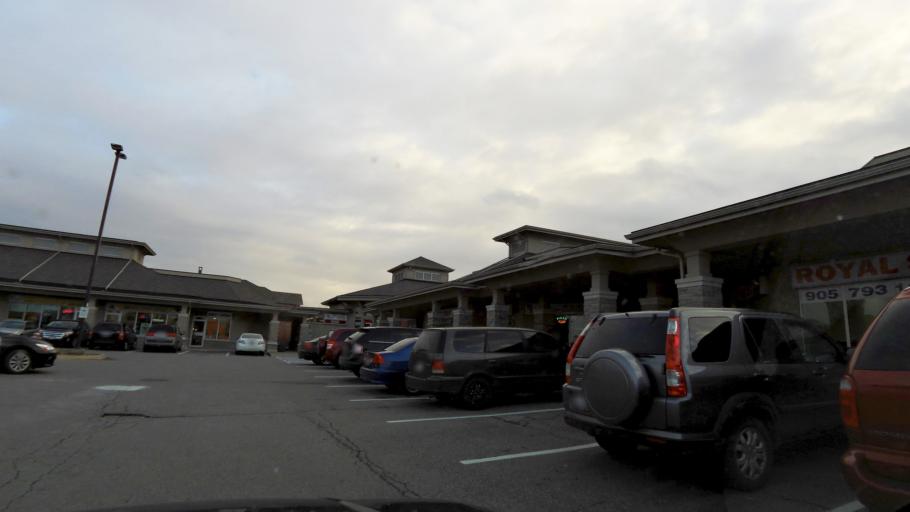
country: CA
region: Ontario
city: Brampton
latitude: 43.7571
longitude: -79.7298
